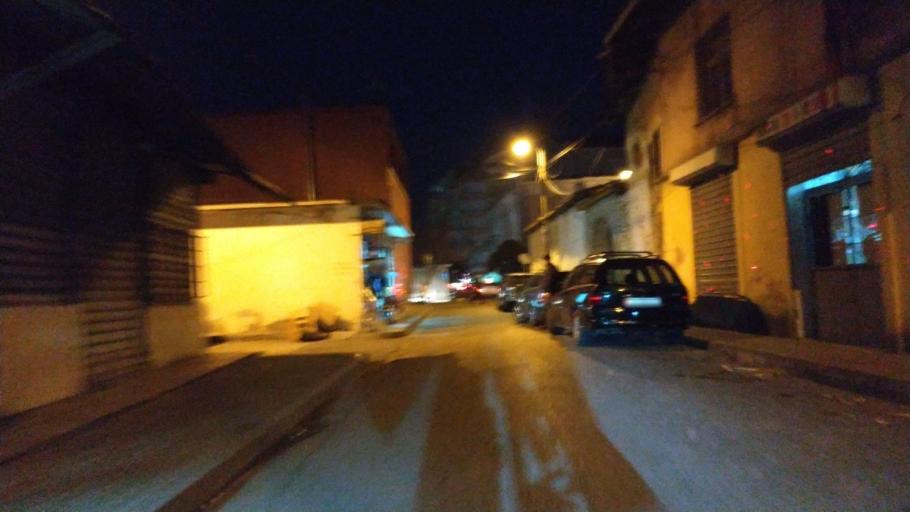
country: AL
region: Shkoder
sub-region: Rrethi i Shkodres
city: Shkoder
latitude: 42.0686
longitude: 19.5099
